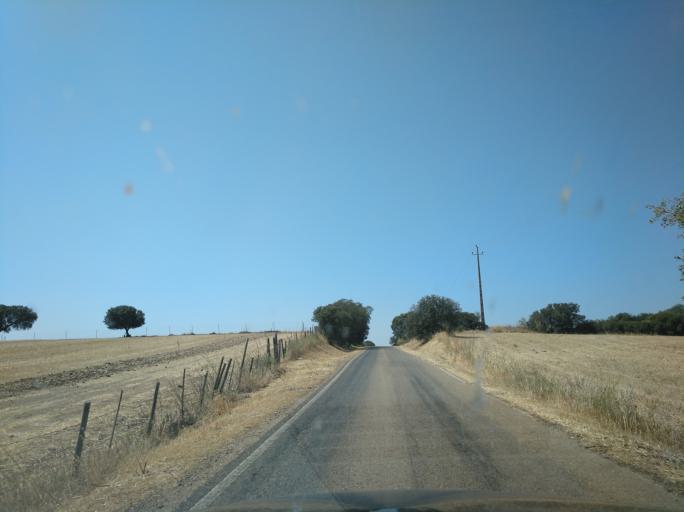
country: PT
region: Portalegre
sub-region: Campo Maior
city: Campo Maior
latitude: 38.9980
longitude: -6.9921
